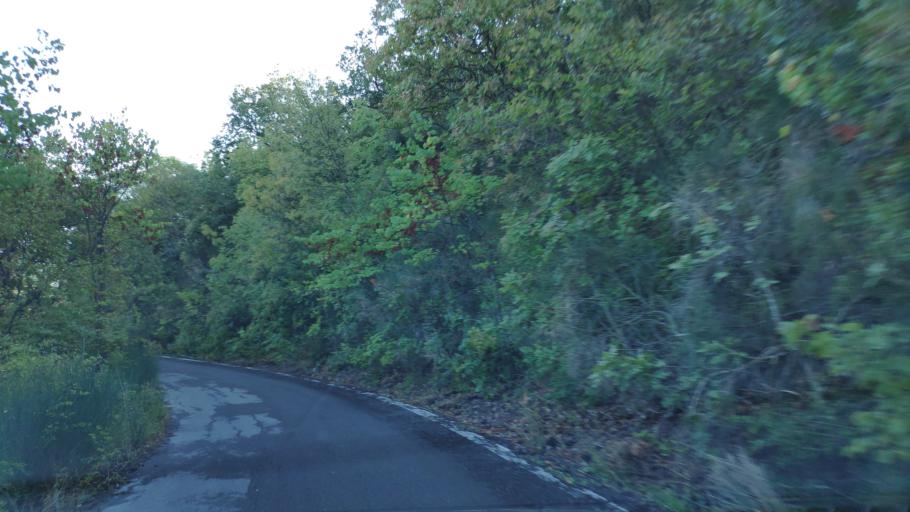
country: GR
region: Peloponnese
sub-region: Nomos Arkadias
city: Dimitsana
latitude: 37.5571
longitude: 22.0403
